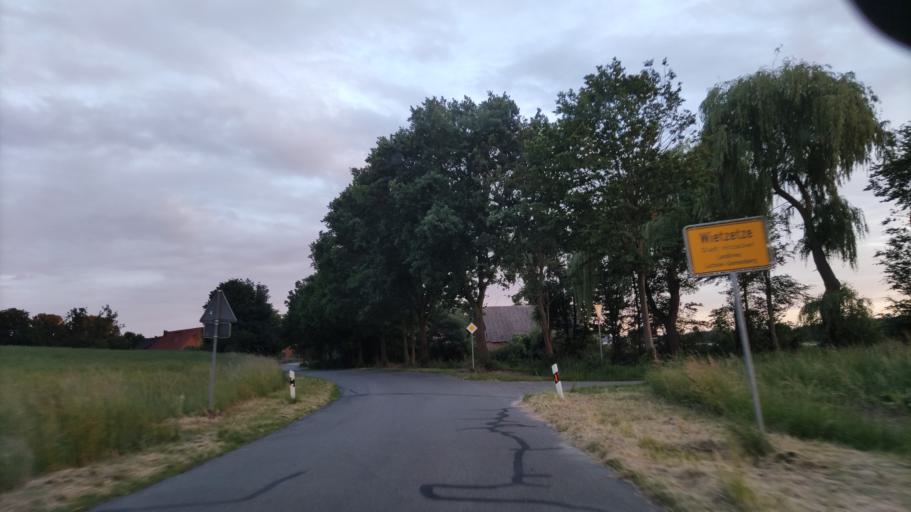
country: DE
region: Lower Saxony
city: Neu Darchau
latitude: 53.1897
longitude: 10.9307
